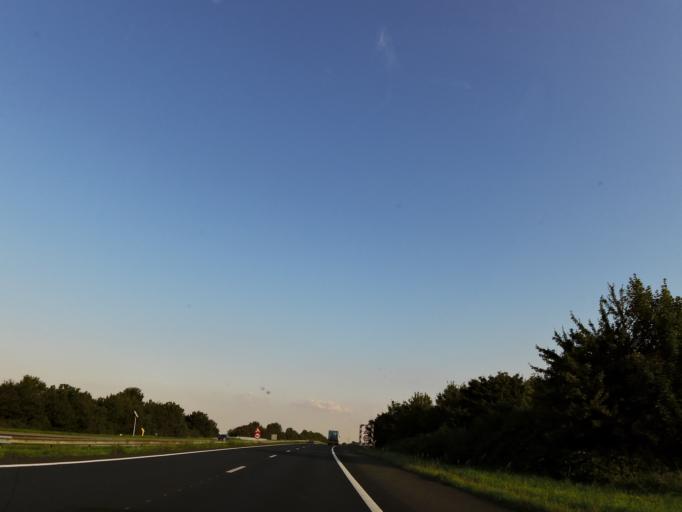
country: NL
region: Zeeland
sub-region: Gemeente Borsele
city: Borssele
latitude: 51.4956
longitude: 3.7816
